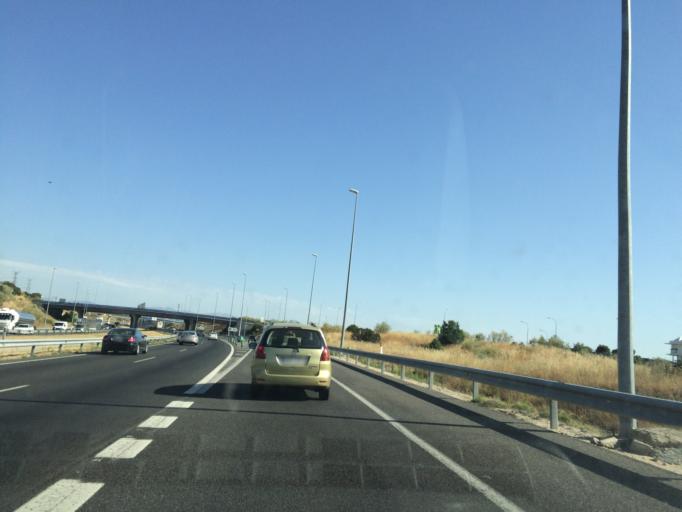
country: ES
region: Madrid
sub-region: Provincia de Madrid
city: Majadahonda
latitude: 40.4404
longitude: -3.8773
